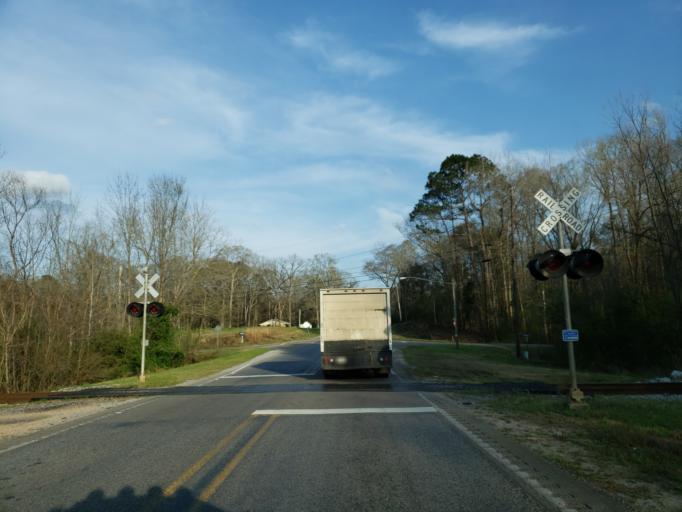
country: US
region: Mississippi
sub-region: Clarke County
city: Stonewall
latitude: 32.1761
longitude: -88.8139
